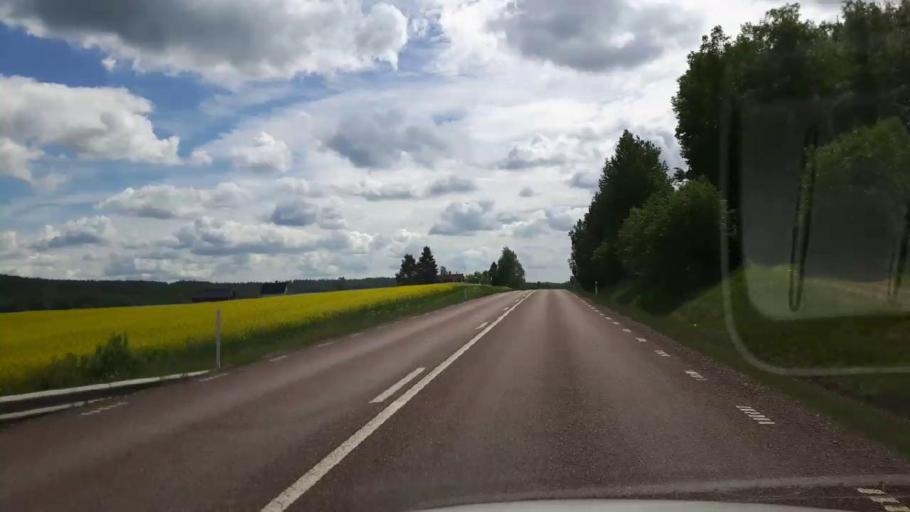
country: SE
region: Dalarna
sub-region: Hedemora Kommun
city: Hedemora
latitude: 60.3793
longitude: 15.9114
